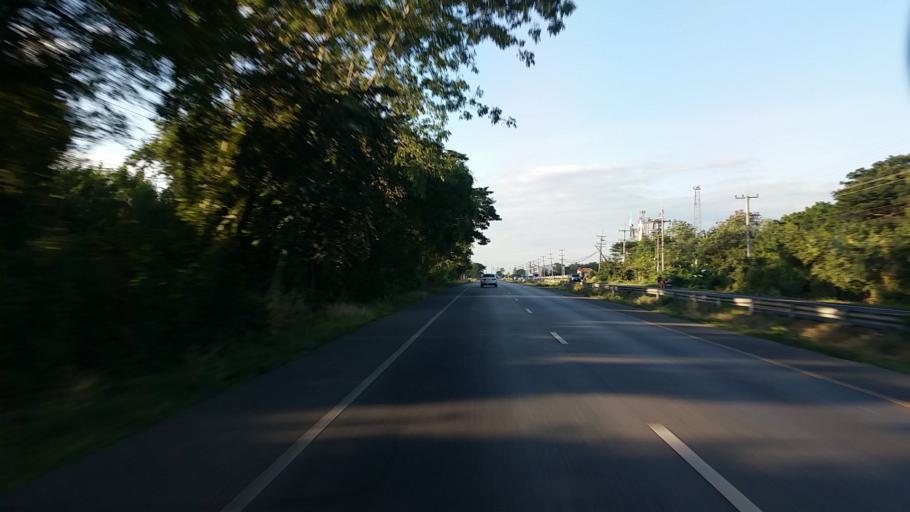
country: TH
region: Lop Buri
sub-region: Amphoe Tha Luang
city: Tha Luang
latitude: 15.0971
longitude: 101.0175
